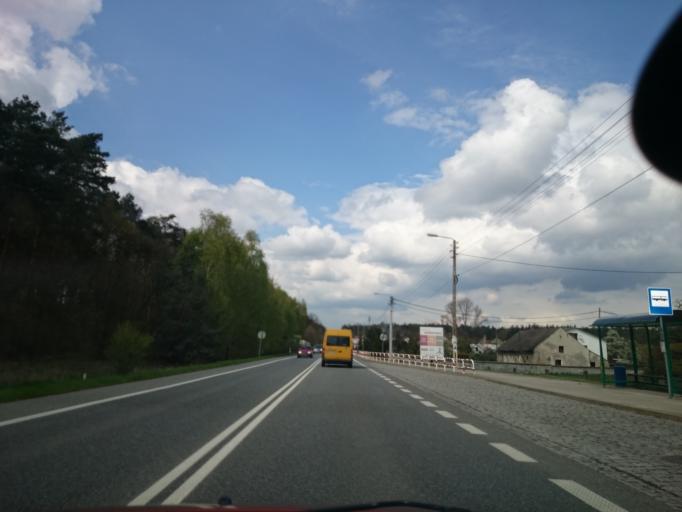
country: PL
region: Opole Voivodeship
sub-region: Powiat opolski
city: Tarnow Opolski
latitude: 50.6079
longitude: 18.0727
